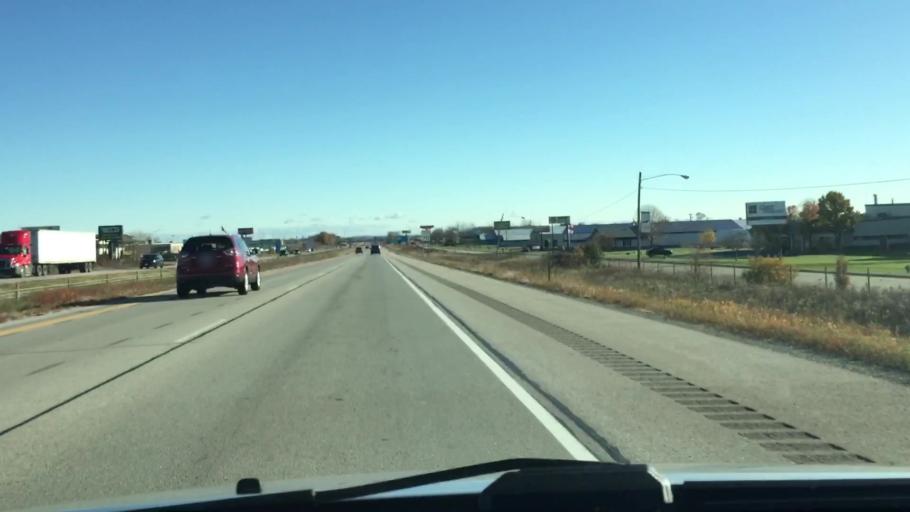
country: US
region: Wisconsin
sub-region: Outagamie County
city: Kaukauna
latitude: 44.3016
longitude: -88.2636
